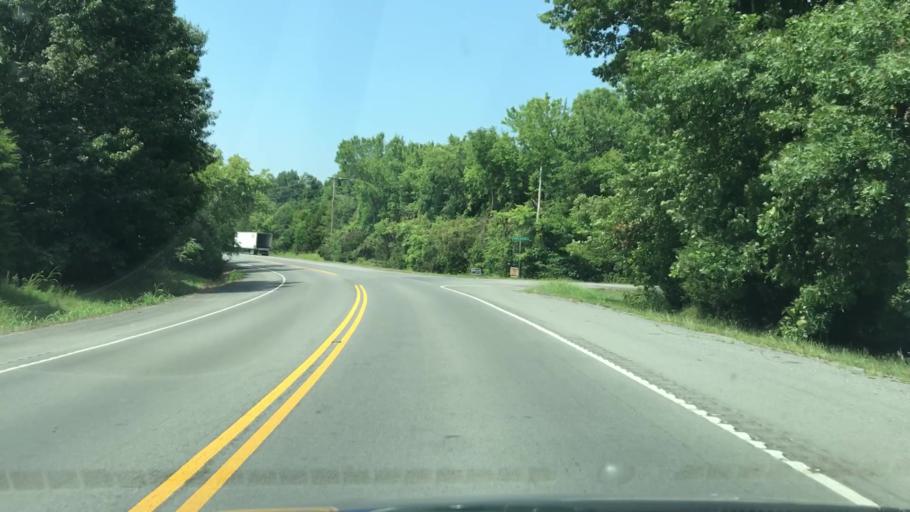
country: US
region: Tennessee
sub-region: Wilson County
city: Rural Hill
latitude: 36.1090
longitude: -86.5486
